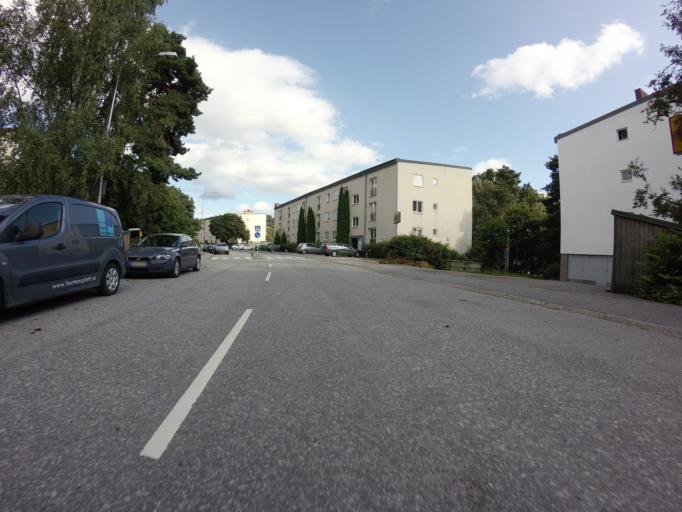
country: SE
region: Stockholm
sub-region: Lidingo
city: Lidingoe
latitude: 59.3746
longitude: 18.1405
